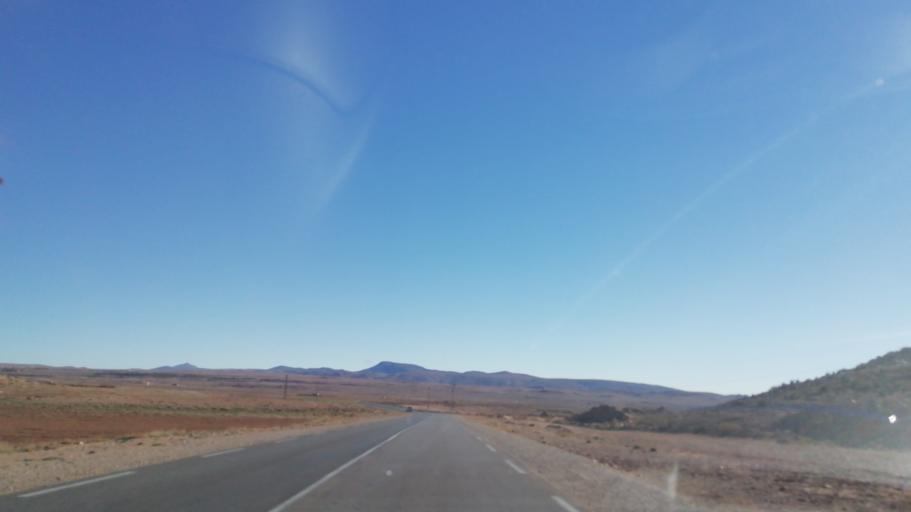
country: DZ
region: El Bayadh
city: El Bayadh
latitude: 33.6037
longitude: 1.2860
